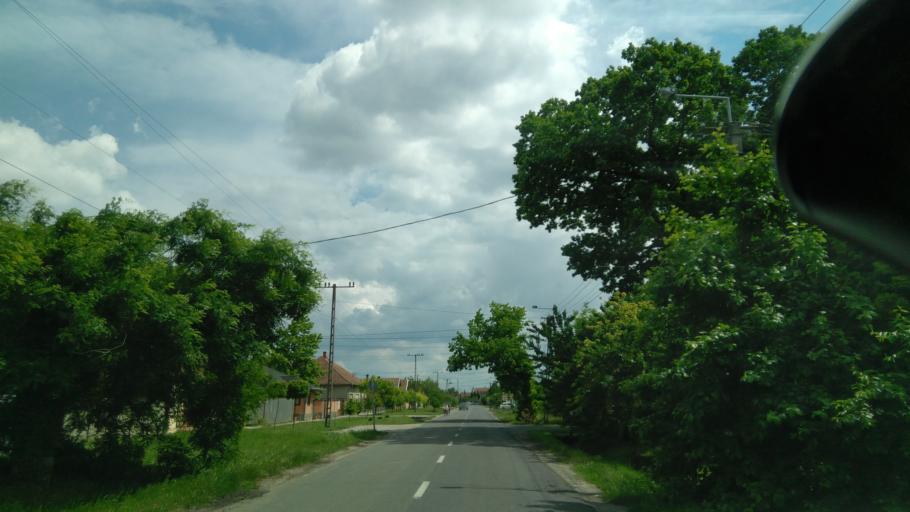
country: HU
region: Bekes
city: Totkomlos
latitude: 46.4091
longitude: 20.7430
